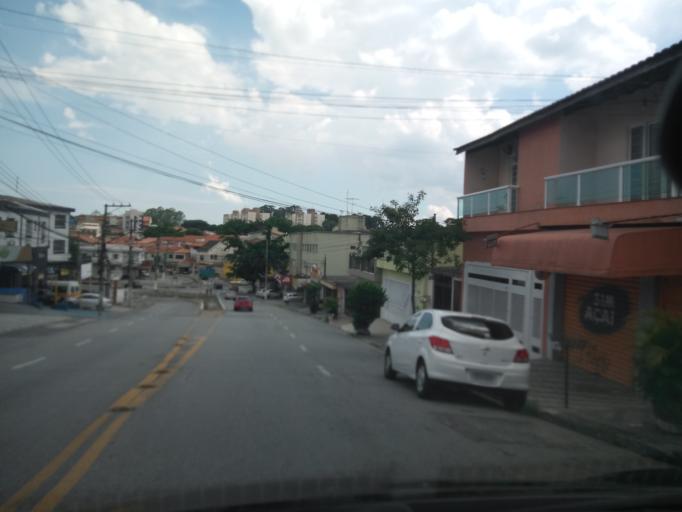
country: BR
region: Sao Paulo
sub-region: Sao Bernardo Do Campo
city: Sao Bernardo do Campo
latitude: -23.7278
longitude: -46.5702
